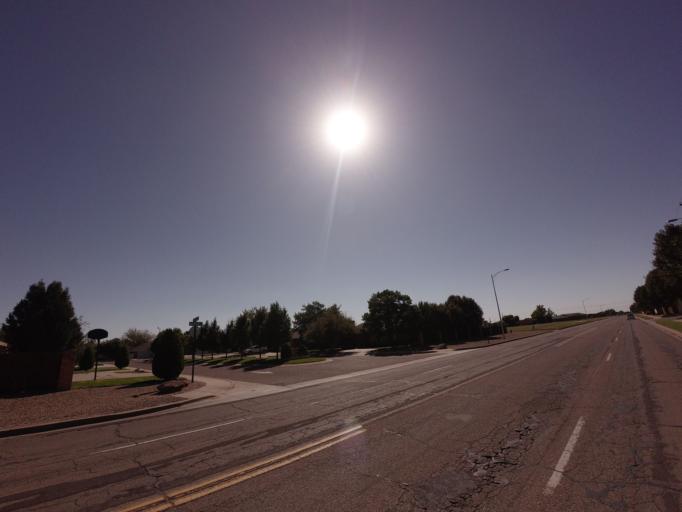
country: US
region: New Mexico
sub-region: Curry County
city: Clovis
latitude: 34.4290
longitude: -103.1786
